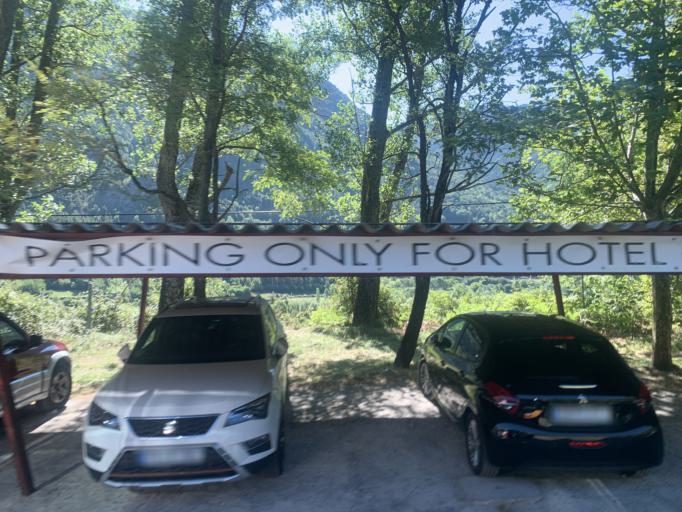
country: ES
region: Aragon
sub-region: Provincia de Huesca
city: Broto
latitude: 42.6387
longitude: -0.1098
